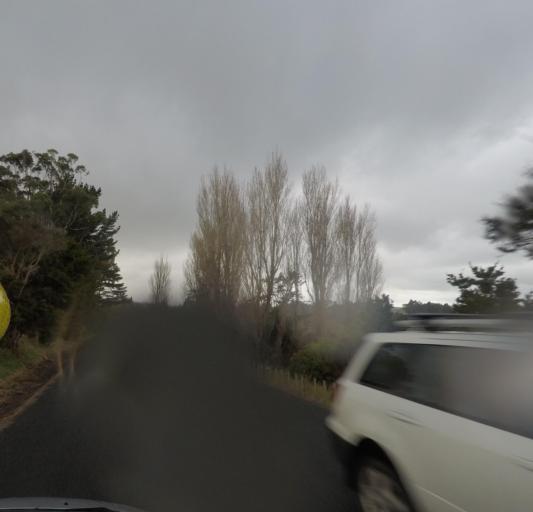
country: NZ
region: Auckland
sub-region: Auckland
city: Warkworth
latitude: -36.3751
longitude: 174.7609
